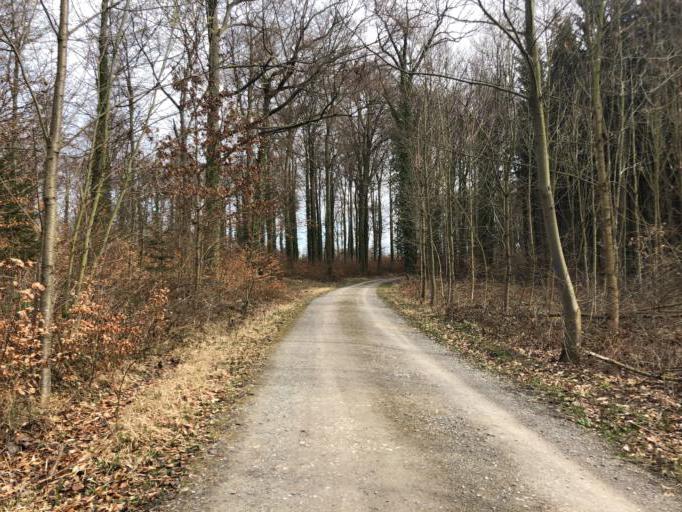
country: DE
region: Baden-Wuerttemberg
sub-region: Karlsruhe Region
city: Wiernsheim
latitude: 48.9226
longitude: 8.8797
